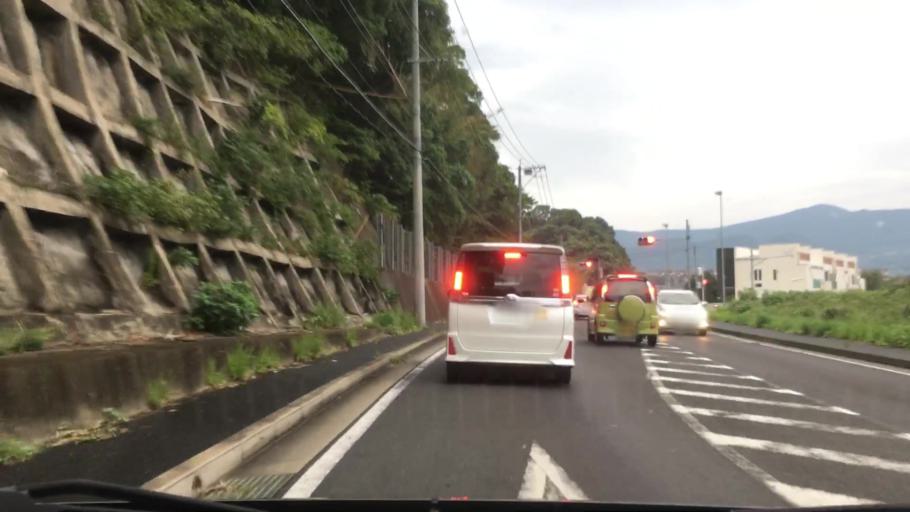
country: JP
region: Nagasaki
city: Sasebo
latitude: 33.1260
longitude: 129.7923
